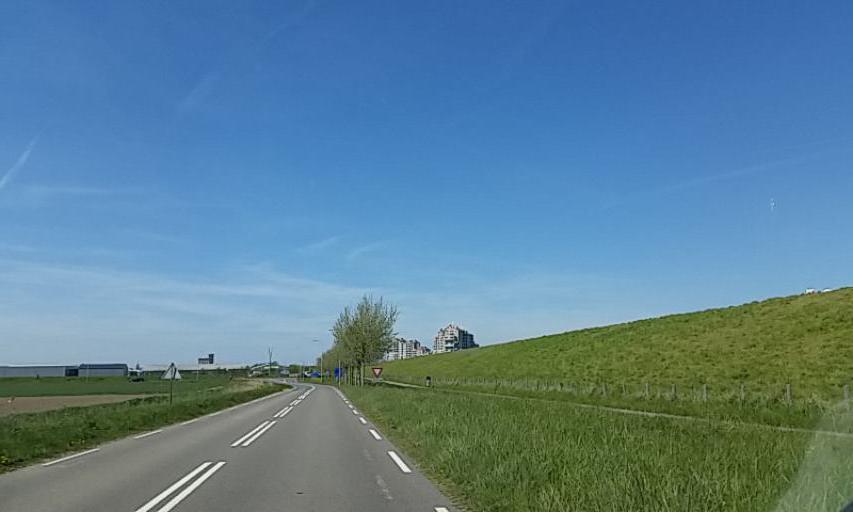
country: NL
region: Zeeland
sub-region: Gemeente Vlissingen
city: Vlissingen
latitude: 51.3883
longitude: 3.5828
